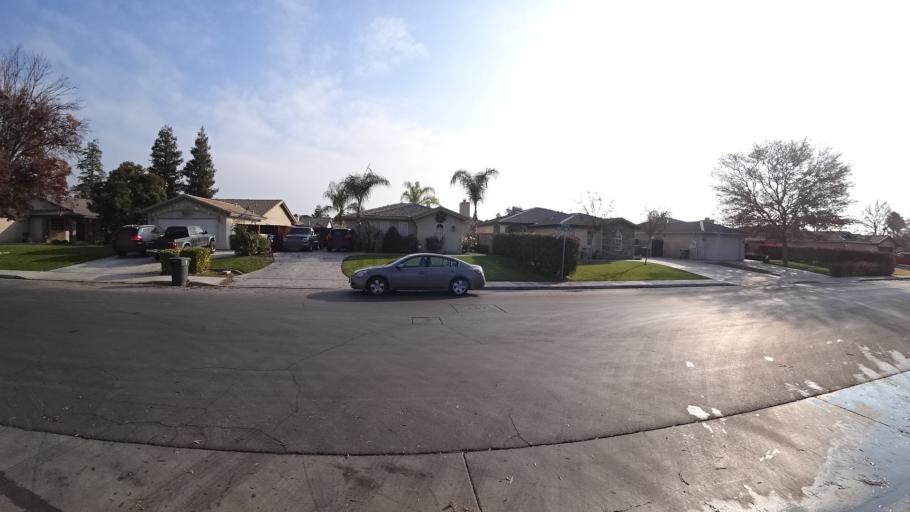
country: US
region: California
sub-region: Kern County
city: Greenfield
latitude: 35.3054
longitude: -119.0659
